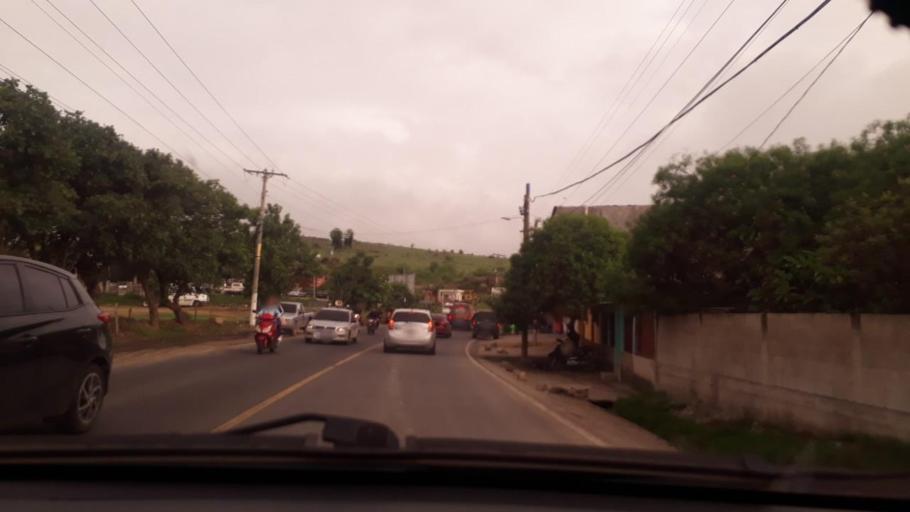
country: GT
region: Jalapa
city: Jalapa
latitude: 14.6493
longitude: -89.9985
